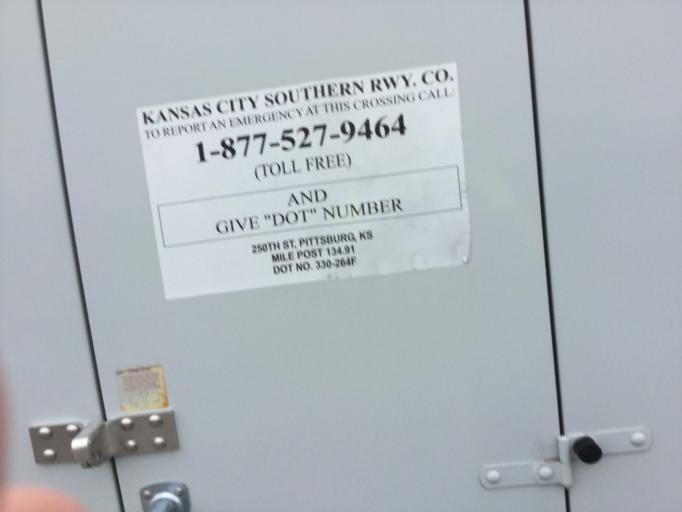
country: US
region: Kansas
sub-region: Crawford County
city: Pittsburg
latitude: 37.3425
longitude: -94.6502
